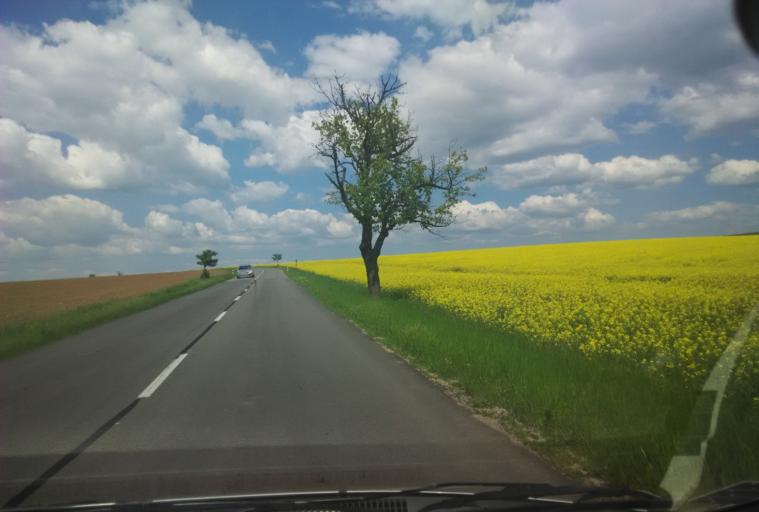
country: SK
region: Banskobystricky
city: Dudince
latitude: 48.2220
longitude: 18.7725
